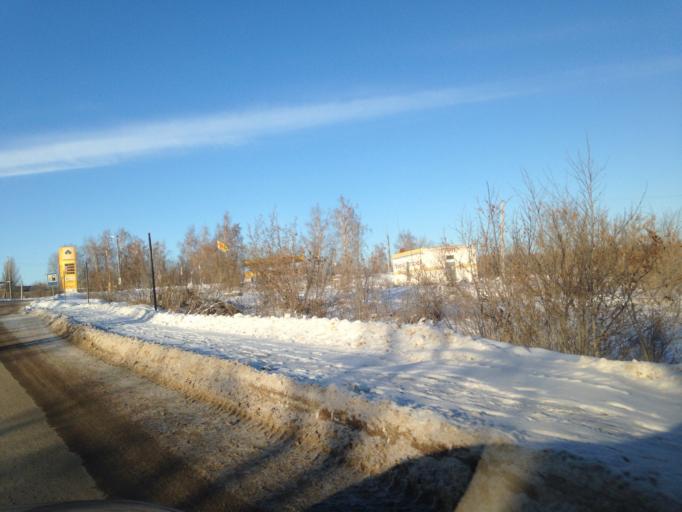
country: RU
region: Ulyanovsk
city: Novoul'yanovsk
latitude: 54.1556
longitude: 48.3697
